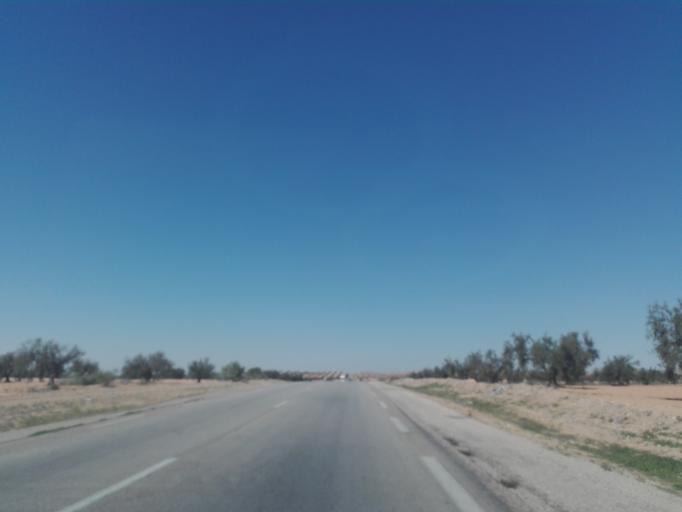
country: TN
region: Safaqis
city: Bi'r `Ali Bin Khalifah
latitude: 34.7586
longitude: 10.2970
